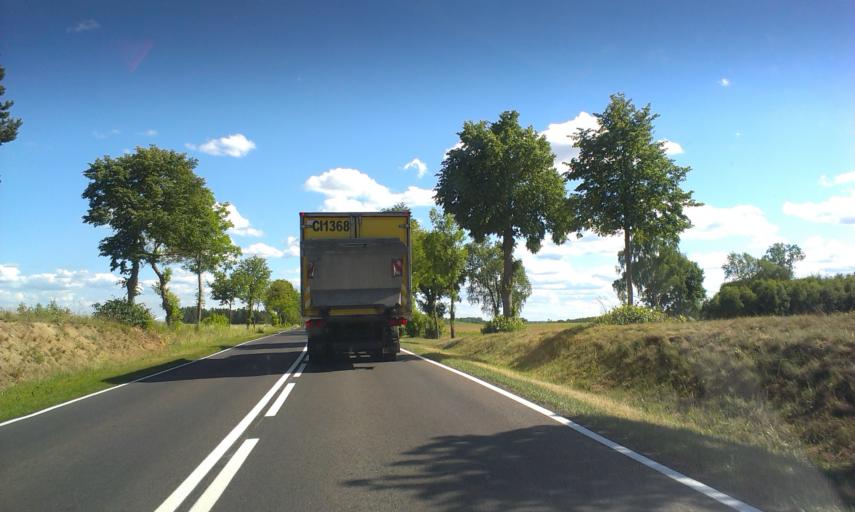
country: PL
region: West Pomeranian Voivodeship
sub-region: Powiat szczecinecki
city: Szczecinek
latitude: 53.7732
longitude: 16.6435
